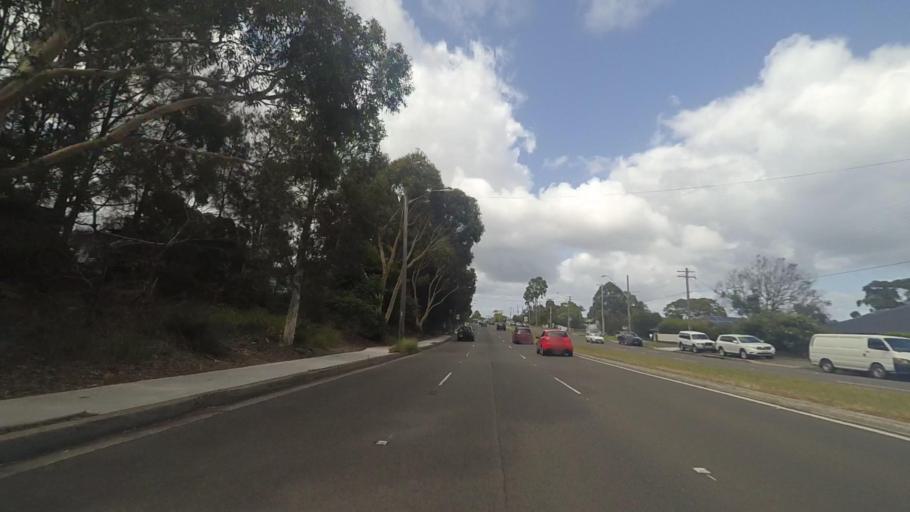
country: AU
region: New South Wales
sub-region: Sutherland Shire
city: Heathcote
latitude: -34.0887
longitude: 151.0064
